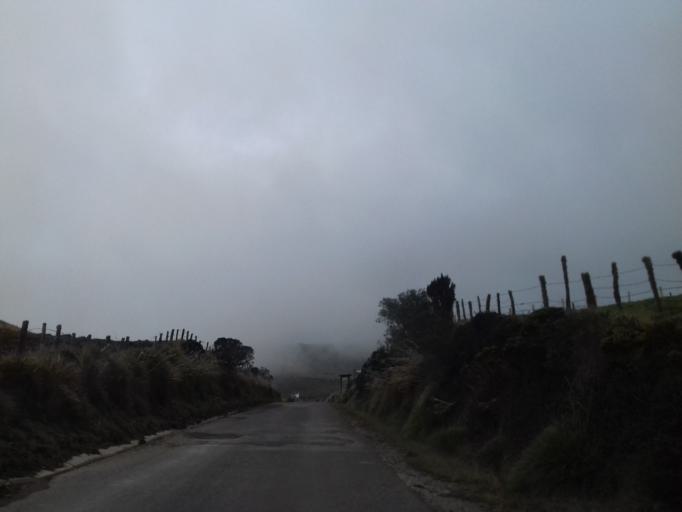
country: CO
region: Caldas
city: Villamaria
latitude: 4.9835
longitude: -75.3350
